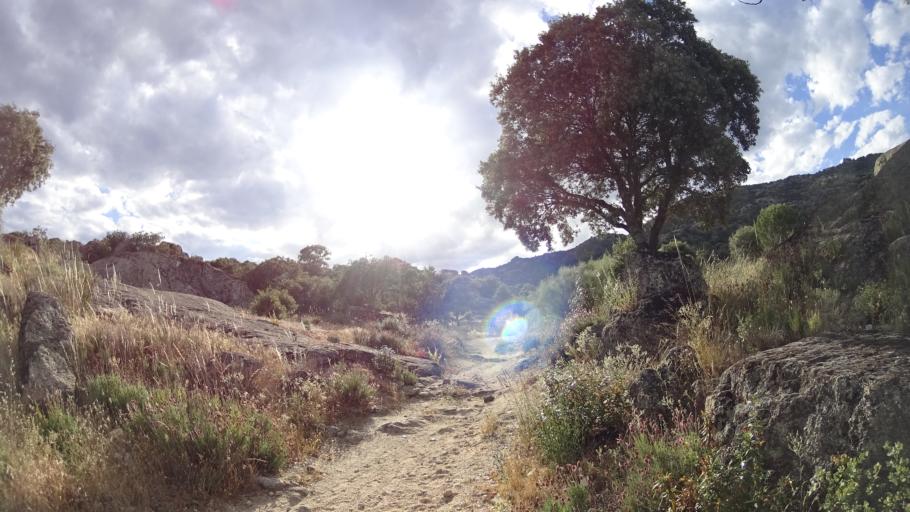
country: ES
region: Madrid
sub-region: Provincia de Madrid
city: Hoyo de Manzanares
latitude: 40.6330
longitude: -3.8970
